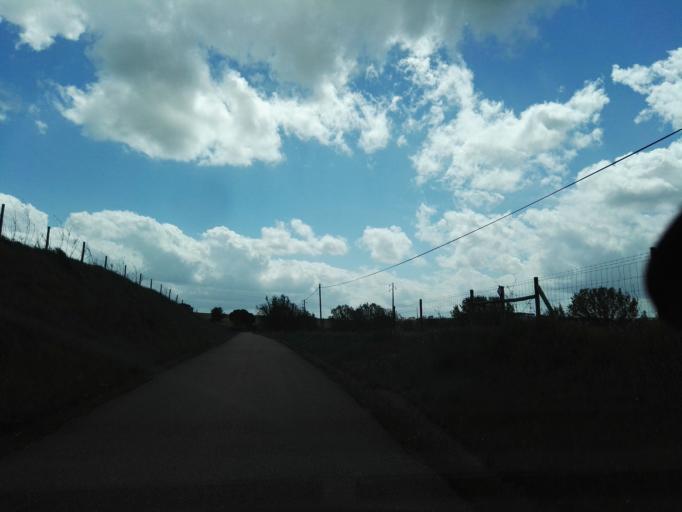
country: PT
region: Portalegre
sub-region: Elvas
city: Elvas
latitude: 38.9695
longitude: -7.1724
